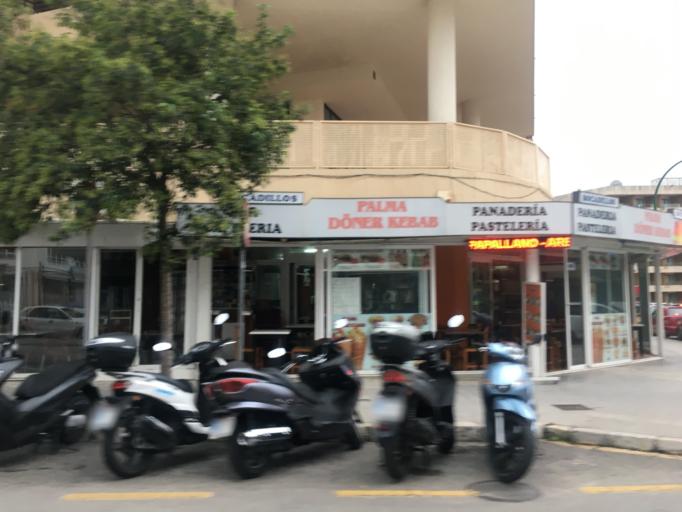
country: ES
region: Balearic Islands
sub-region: Illes Balears
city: Palma
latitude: 39.5656
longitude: 2.6267
